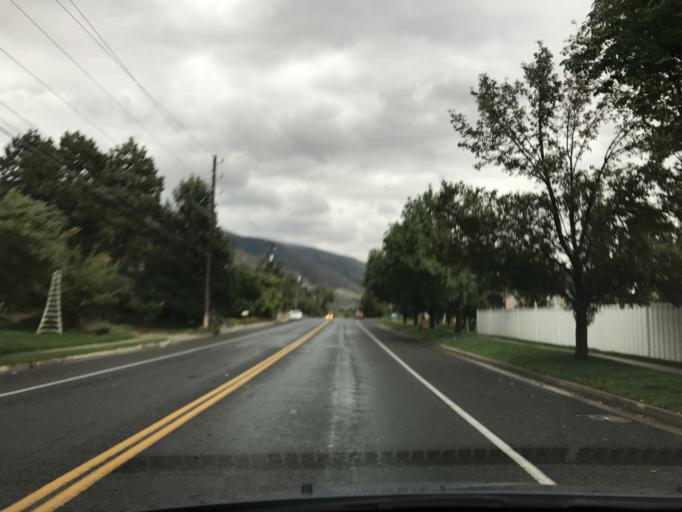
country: US
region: Utah
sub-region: Davis County
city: Fruit Heights
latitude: 41.0048
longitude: -111.9045
